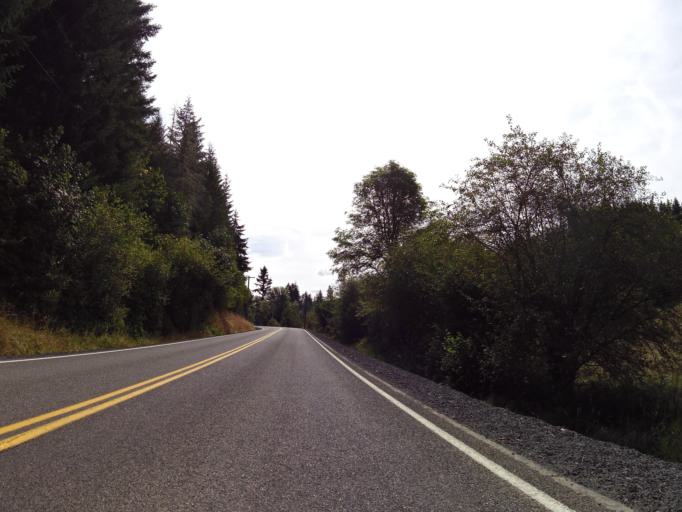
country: US
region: Washington
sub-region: Lewis County
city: Napavine
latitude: 46.5688
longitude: -122.9676
